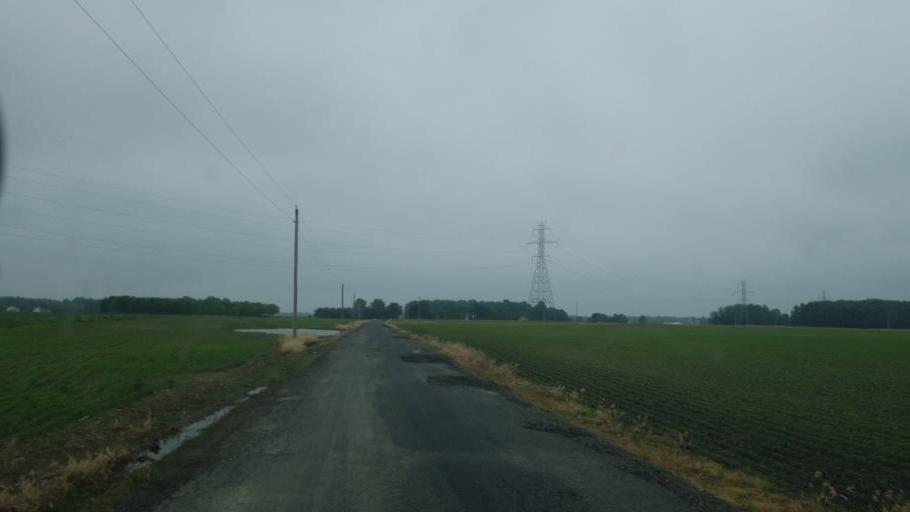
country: US
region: Indiana
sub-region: Marshall County
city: Bremen
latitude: 41.4794
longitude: -86.1307
